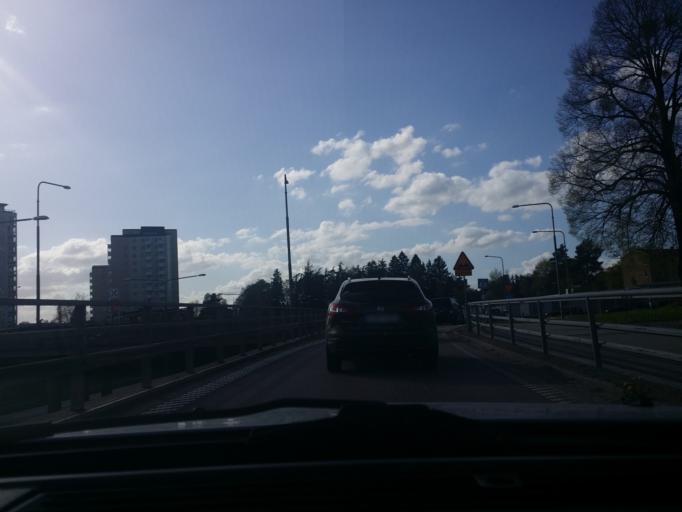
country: SE
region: Vaestmanland
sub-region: Vasteras
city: Vasteras
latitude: 59.6192
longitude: 16.5574
